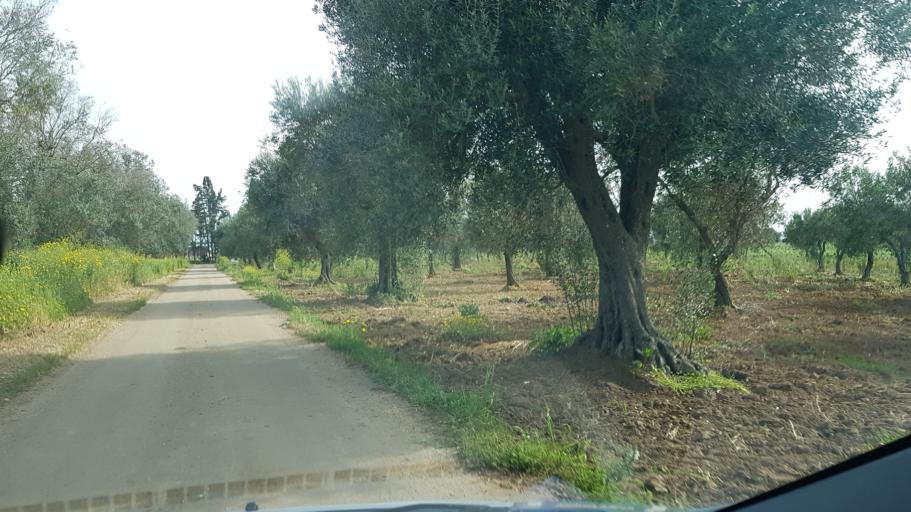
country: IT
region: Apulia
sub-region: Provincia di Brindisi
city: Tuturano
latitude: 40.5625
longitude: 17.9179
